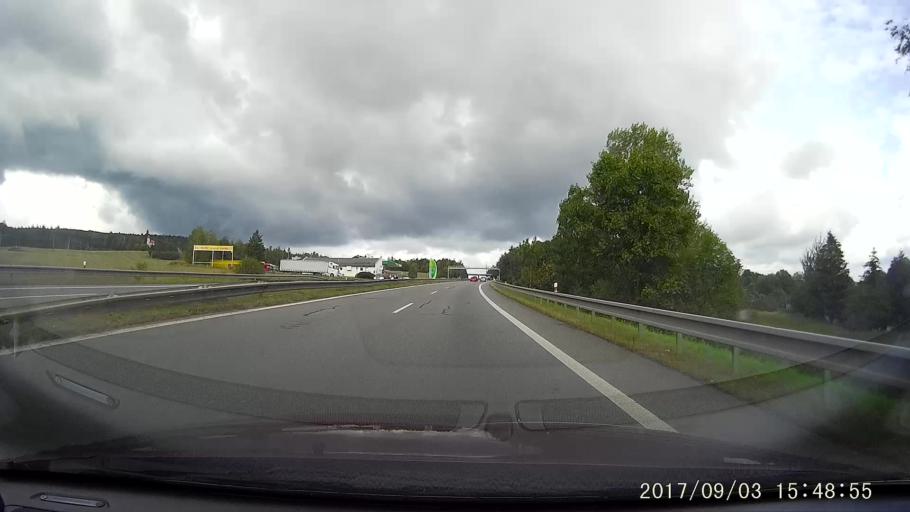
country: CZ
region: Vysocina
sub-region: Okres Jihlava
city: Jihlava
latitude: 49.4197
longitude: 15.5802
